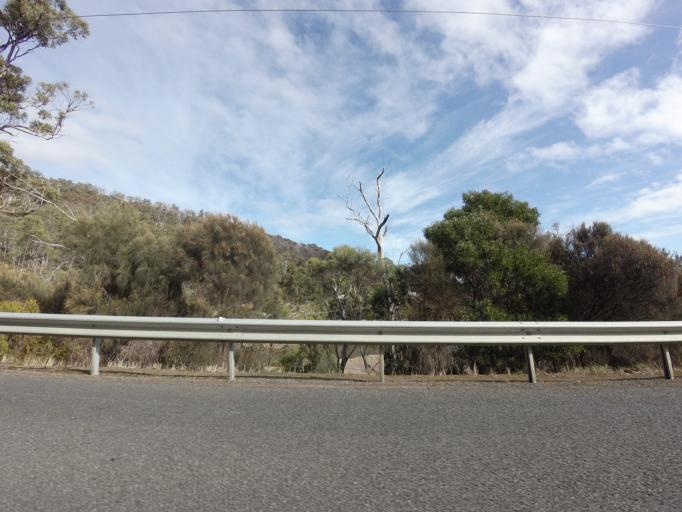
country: AU
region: Tasmania
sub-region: Clarence
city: Sandford
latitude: -43.1107
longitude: 147.7466
